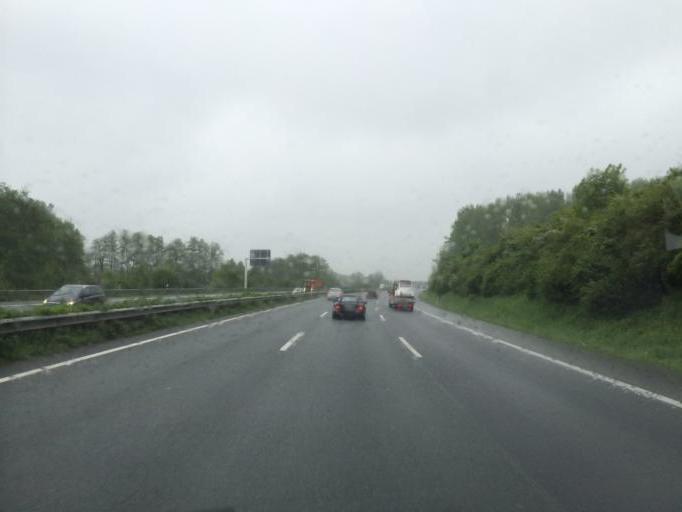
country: DE
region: North Rhine-Westphalia
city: Porta Westfalica
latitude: 52.2112
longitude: 8.8912
